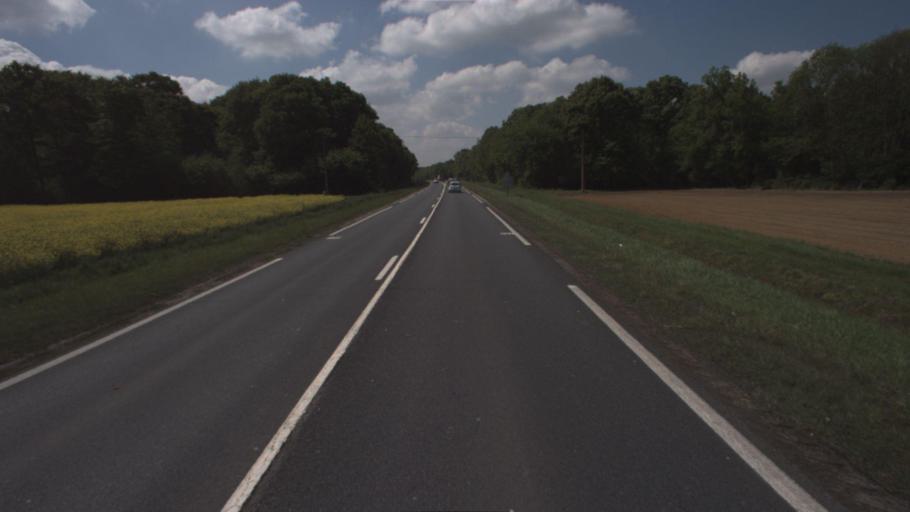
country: FR
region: Ile-de-France
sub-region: Departement de Seine-et-Marne
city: Chaumes-en-Brie
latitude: 48.6980
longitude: 2.8246
